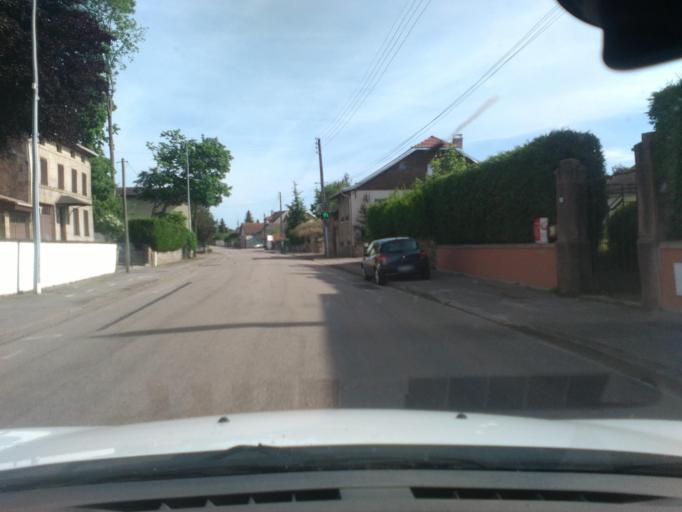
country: FR
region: Lorraine
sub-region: Departement des Vosges
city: Rambervillers
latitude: 48.3529
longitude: 6.6311
